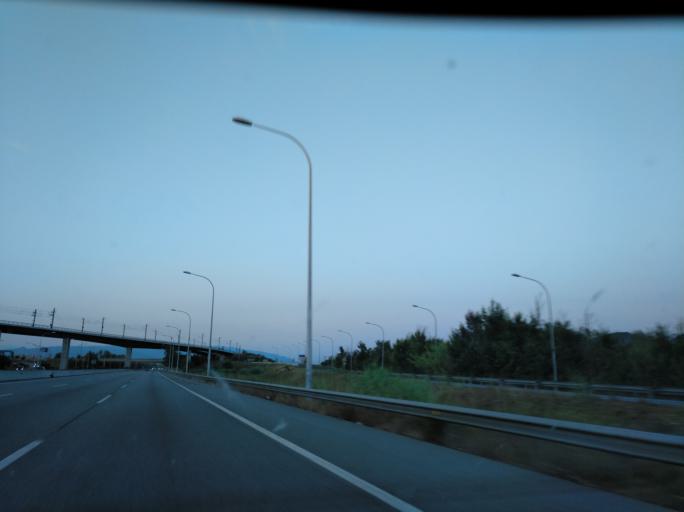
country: ES
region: Catalonia
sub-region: Provincia de Barcelona
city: Mollet del Valles
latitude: 41.5207
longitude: 2.2117
